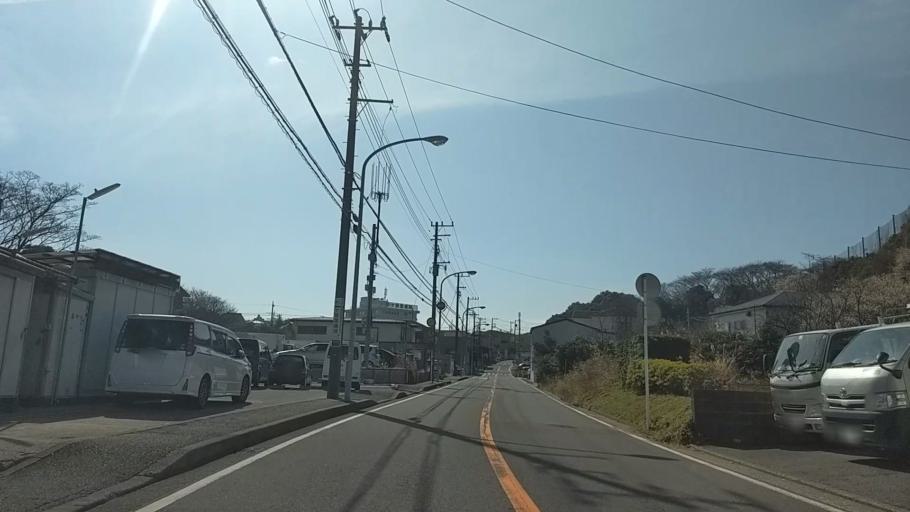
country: JP
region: Kanagawa
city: Kamakura
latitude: 35.3985
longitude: 139.5559
